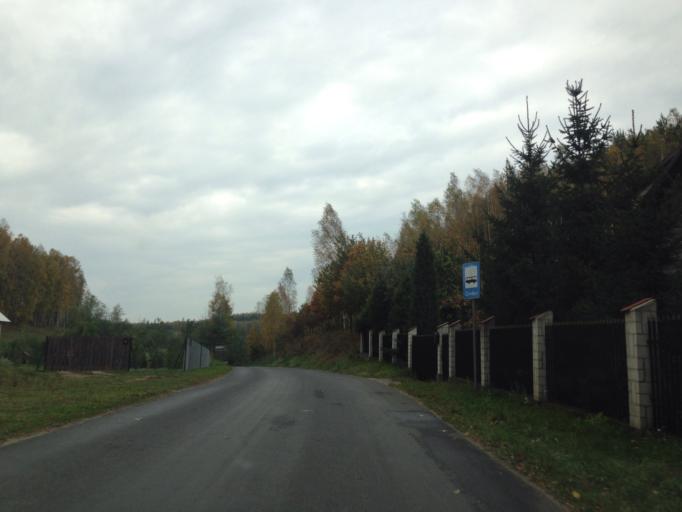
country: PL
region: Kujawsko-Pomorskie
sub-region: Powiat brodnicki
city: Brzozie
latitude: 53.3111
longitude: 19.5672
